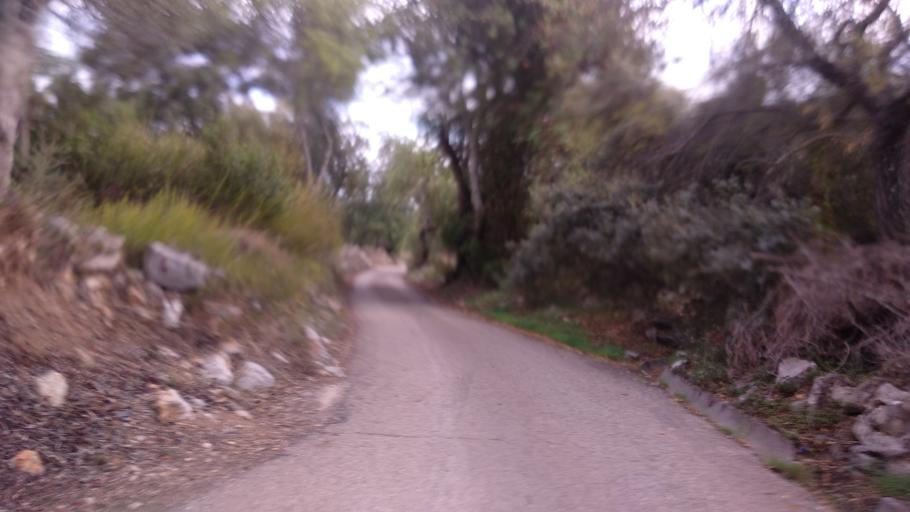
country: PT
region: Faro
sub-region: Sao Bras de Alportel
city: Sao Bras de Alportel
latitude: 37.1574
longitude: -7.8989
